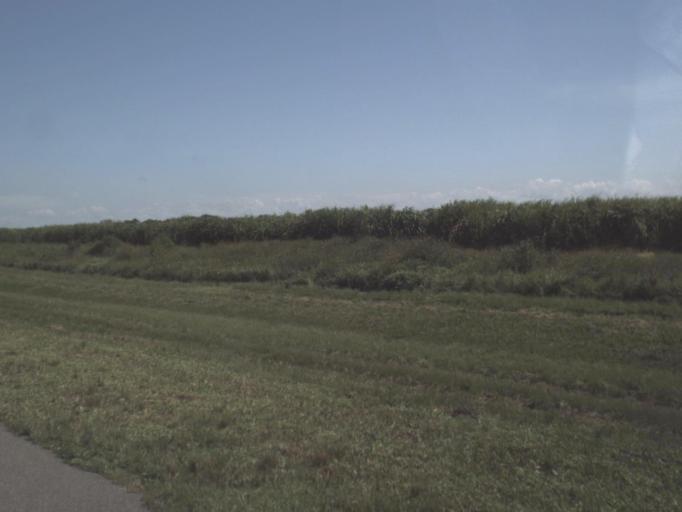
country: US
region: Florida
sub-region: Glades County
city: Moore Haven
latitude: 26.8227
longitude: -81.1967
